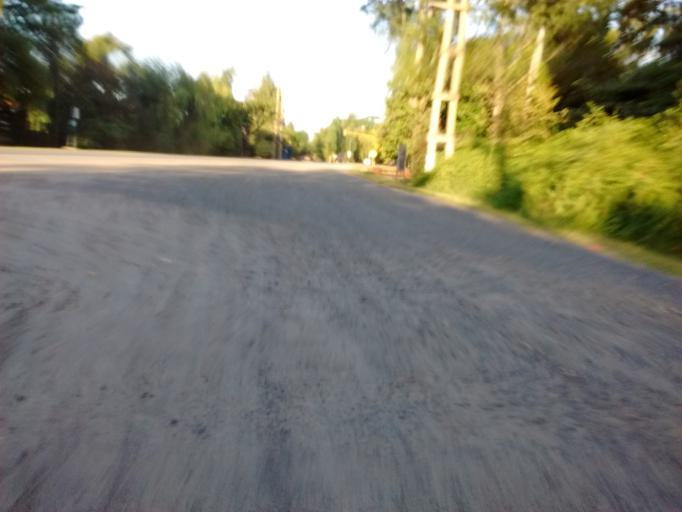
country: AR
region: Santa Fe
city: Funes
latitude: -32.9193
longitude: -60.8250
